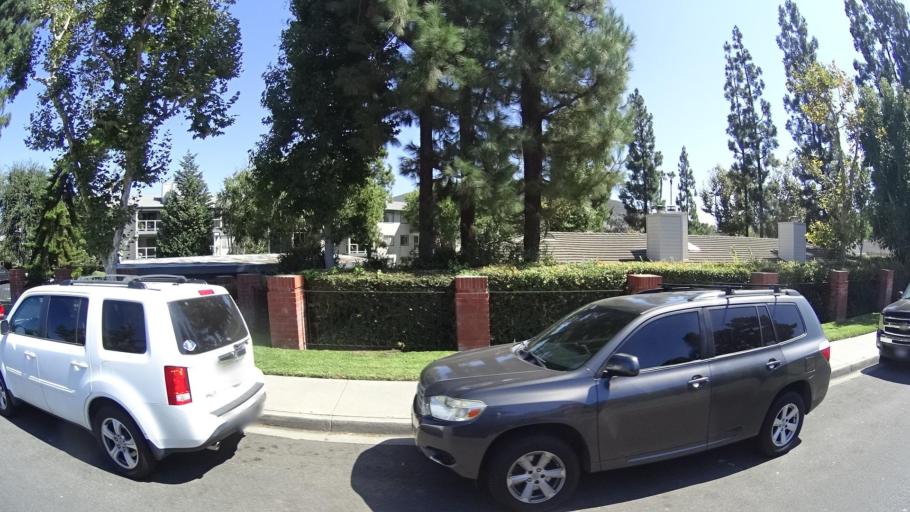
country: US
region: California
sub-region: San Diego County
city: Lake San Marcos
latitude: 33.1232
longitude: -117.2115
